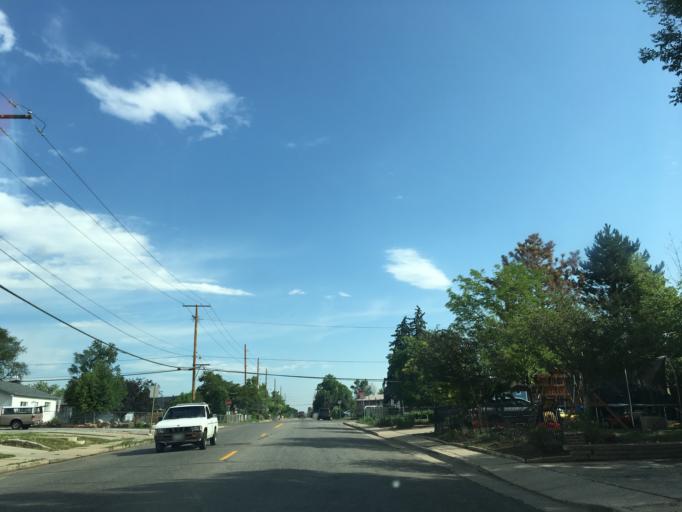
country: US
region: Colorado
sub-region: Arapahoe County
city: Sheridan
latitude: 39.6924
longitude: -105.0296
